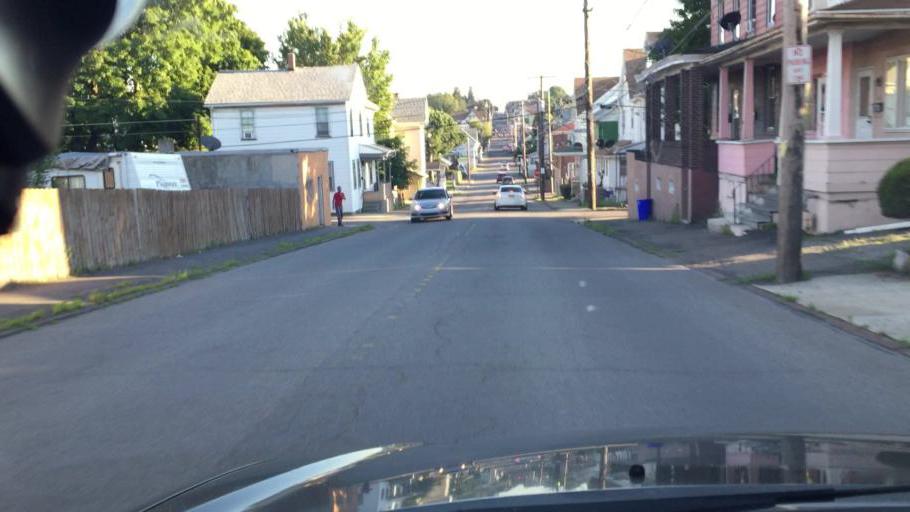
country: US
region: Pennsylvania
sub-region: Luzerne County
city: Hazleton
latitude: 40.9564
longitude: -75.9694
